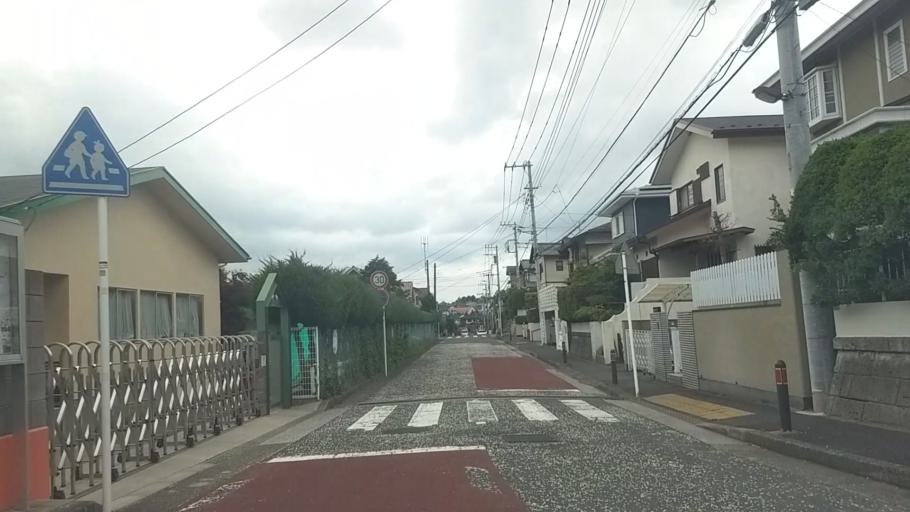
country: JP
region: Kanagawa
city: Fujisawa
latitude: 35.3565
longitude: 139.5062
